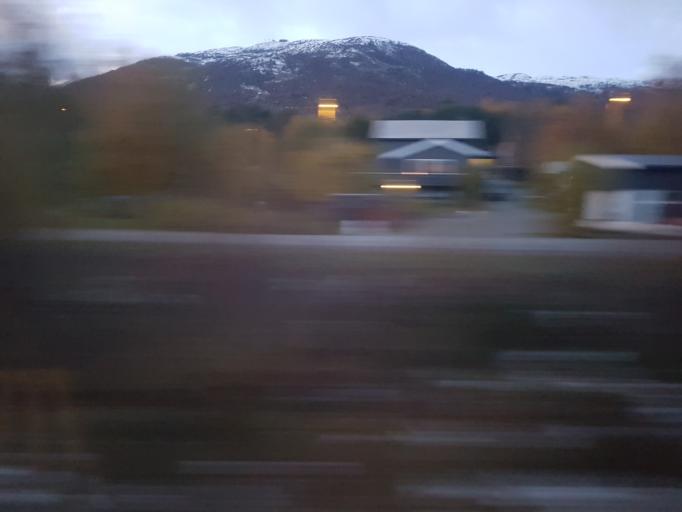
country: NO
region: Sor-Trondelag
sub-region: Oppdal
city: Oppdal
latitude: 62.5982
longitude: 9.7116
